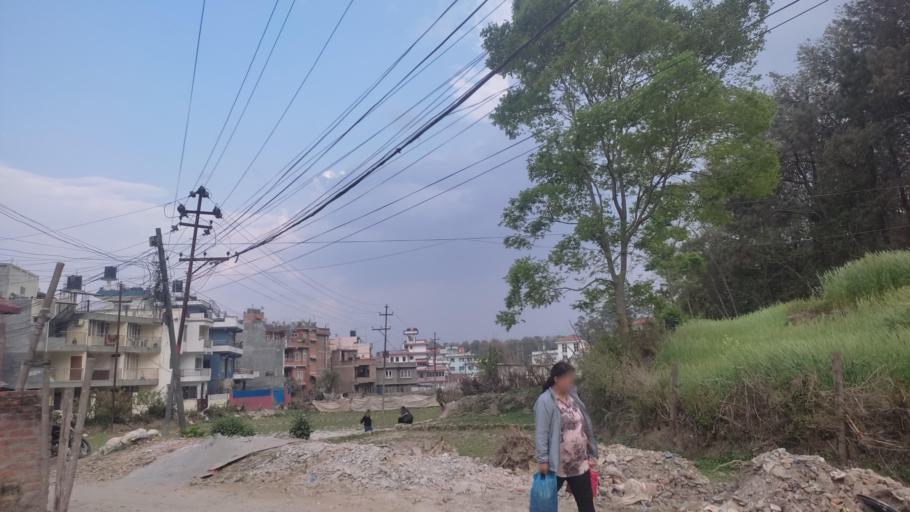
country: NP
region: Central Region
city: Kirtipur
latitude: 27.6811
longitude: 85.2940
